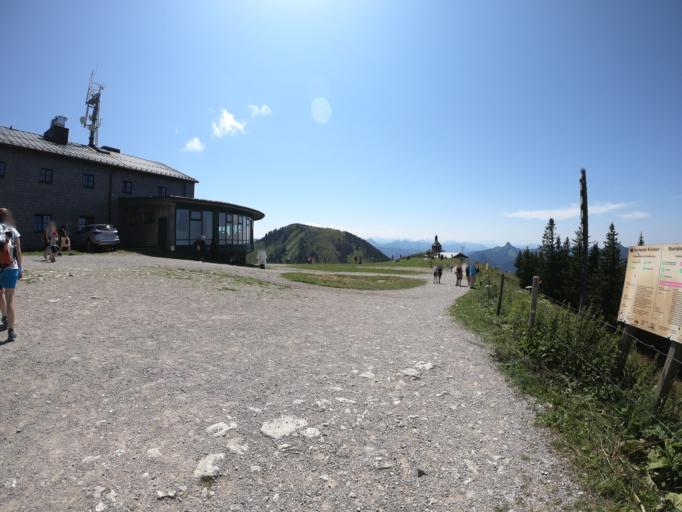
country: DE
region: Bavaria
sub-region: Upper Bavaria
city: Rottach-Egern
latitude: 47.6616
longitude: 11.7935
